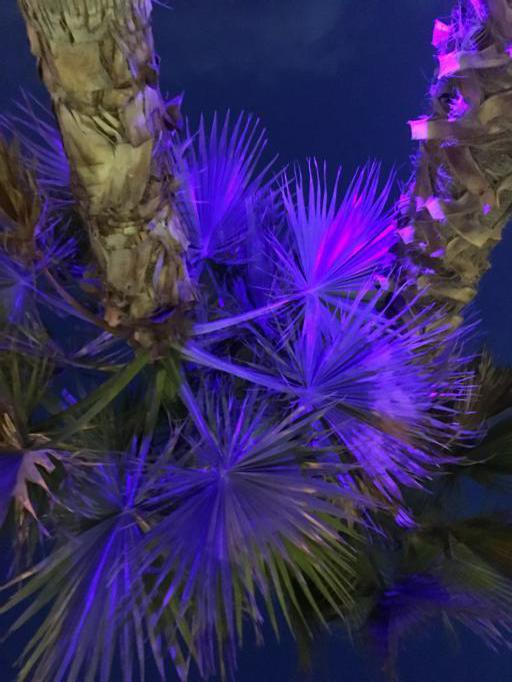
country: AL
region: Tirane
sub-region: Rrethi i Kavajes
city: Golem
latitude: 41.2636
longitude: 19.5195
